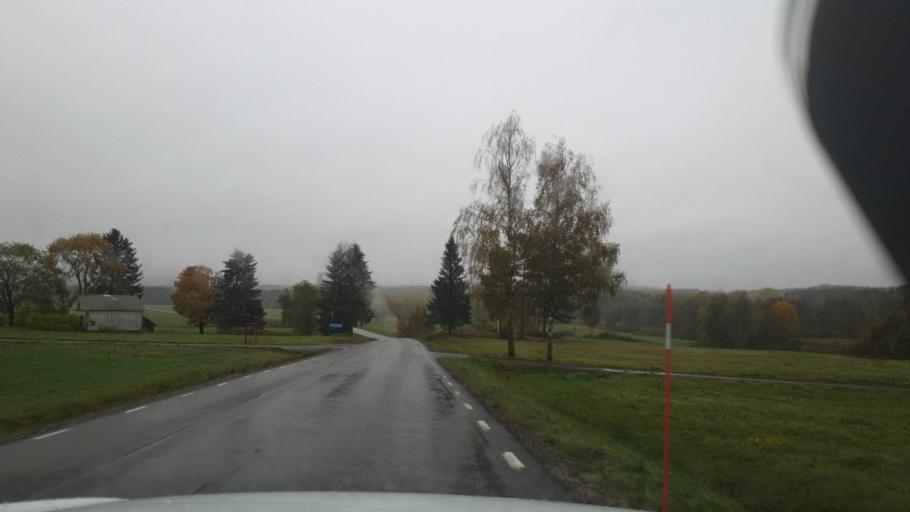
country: SE
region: Vaermland
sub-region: Eda Kommun
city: Charlottenberg
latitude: 59.7856
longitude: 12.1590
